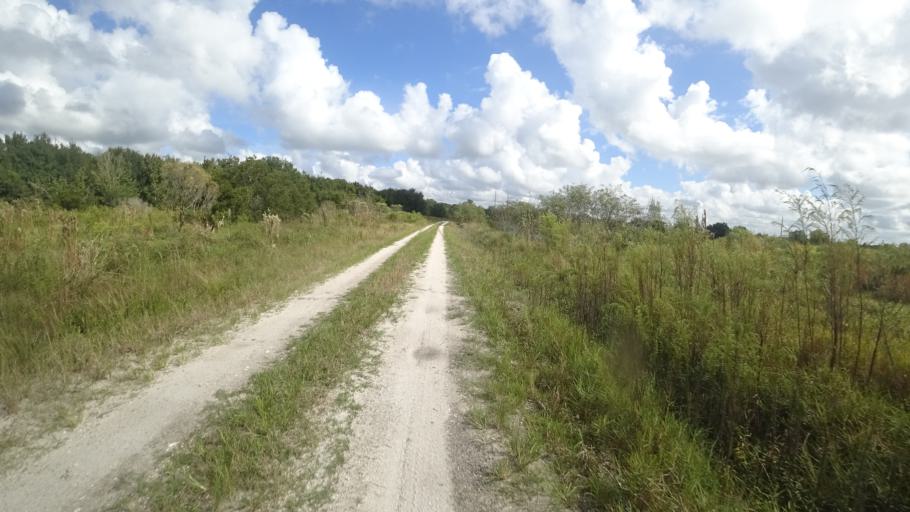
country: US
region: Florida
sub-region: Hillsborough County
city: Wimauma
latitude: 27.5148
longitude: -82.1325
